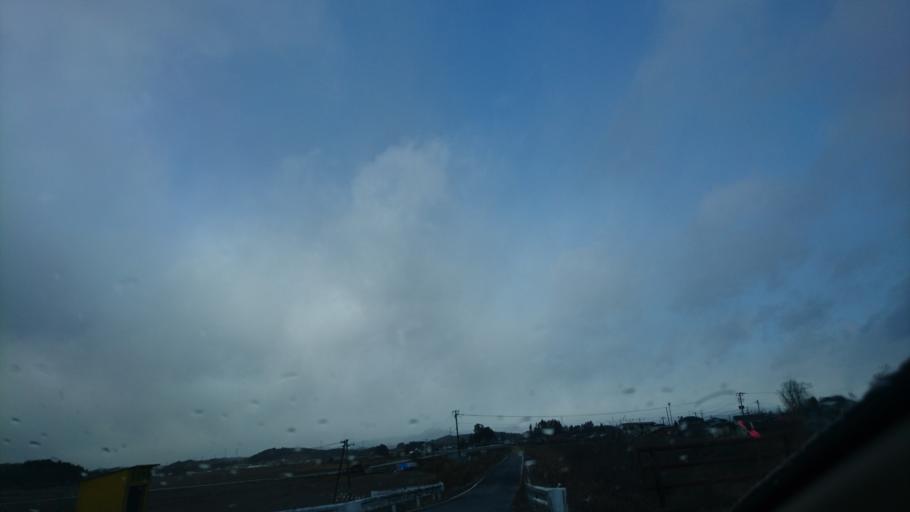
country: JP
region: Iwate
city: Ichinoseki
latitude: 38.7720
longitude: 141.0293
